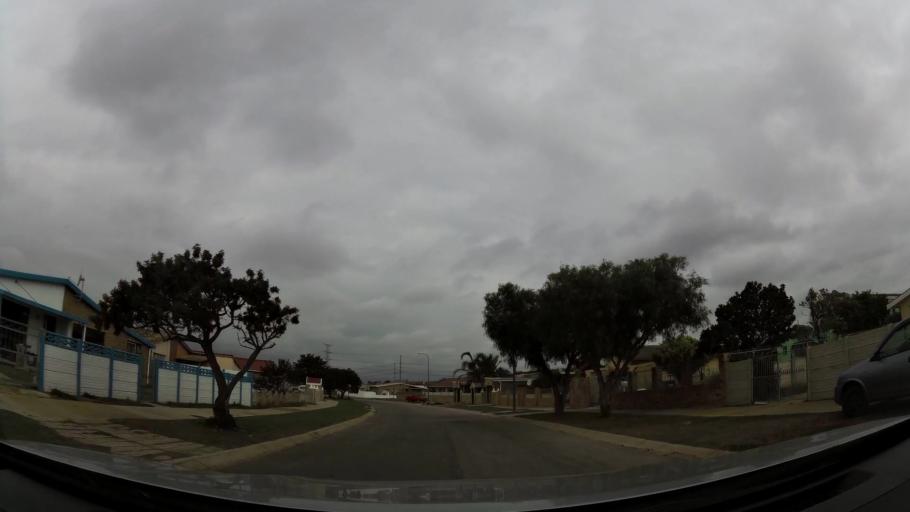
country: ZA
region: Eastern Cape
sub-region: Nelson Mandela Bay Metropolitan Municipality
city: Port Elizabeth
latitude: -33.8993
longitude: 25.5524
